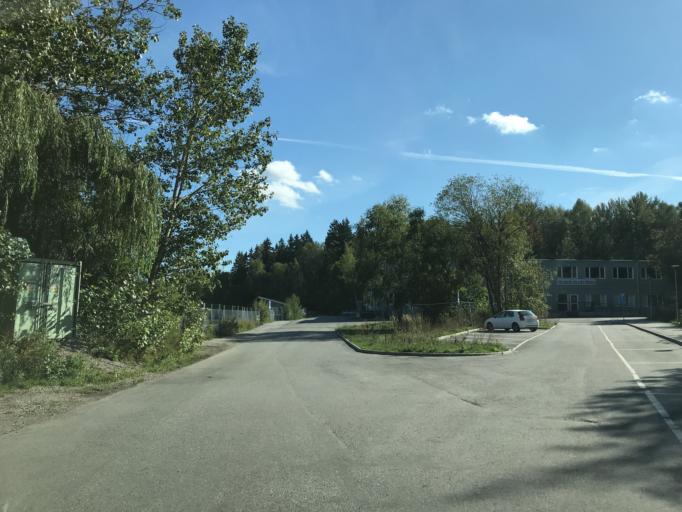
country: SE
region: Stockholm
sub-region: Sollentuna Kommun
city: Sollentuna
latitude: 59.4130
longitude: 17.9849
